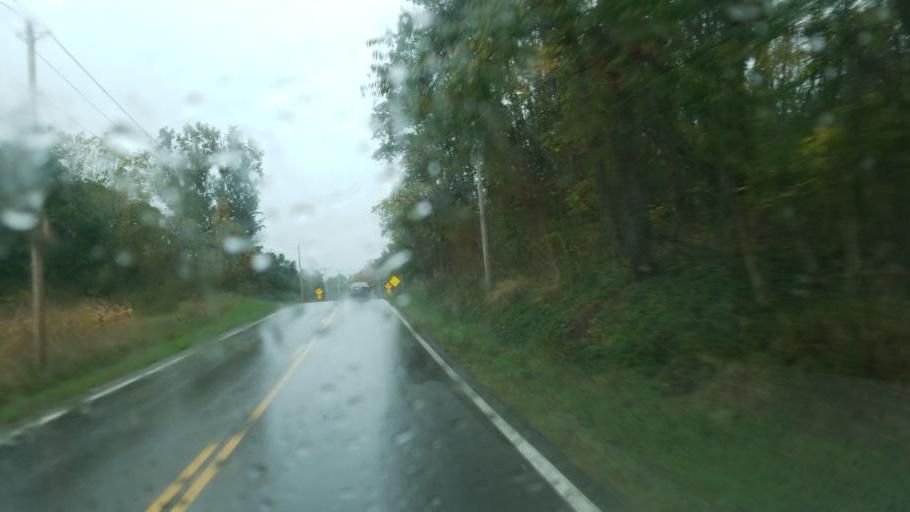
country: US
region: Ohio
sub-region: Richland County
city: Lincoln Heights
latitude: 40.8321
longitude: -82.4771
